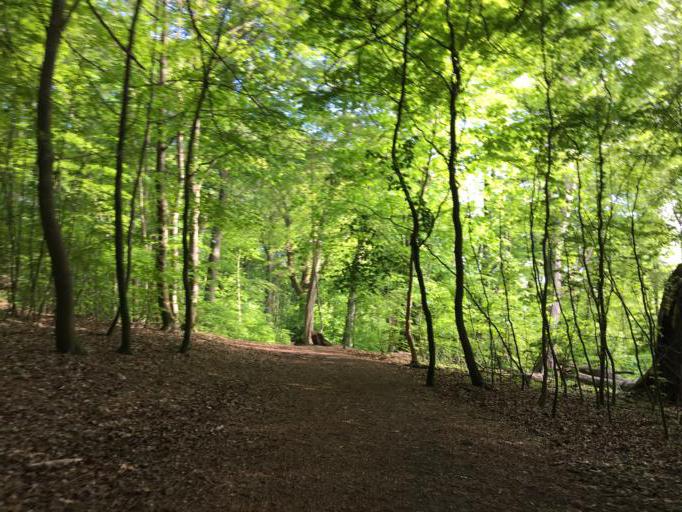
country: DK
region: Capital Region
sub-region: Hillerod Kommune
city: Hillerod
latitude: 55.9265
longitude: 12.3170
